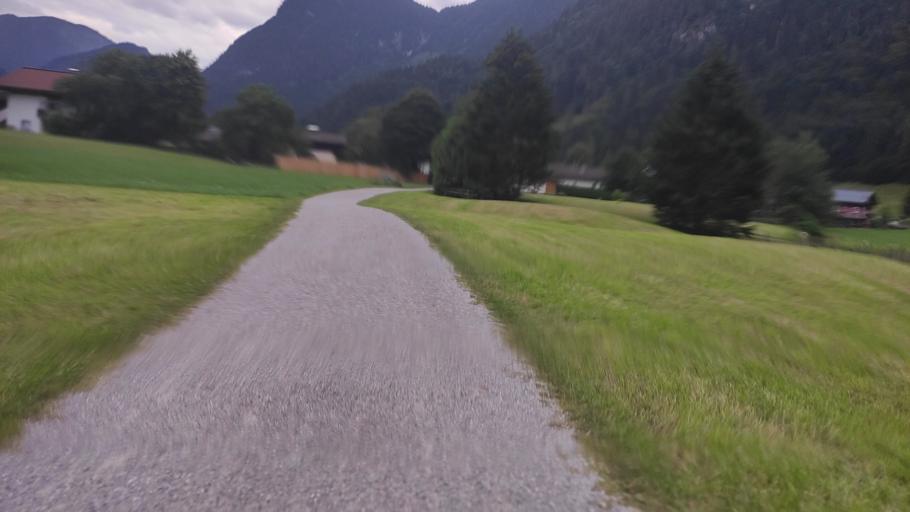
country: AT
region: Salzburg
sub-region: Politischer Bezirk Zell am See
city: Lofer
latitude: 47.5753
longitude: 12.6922
